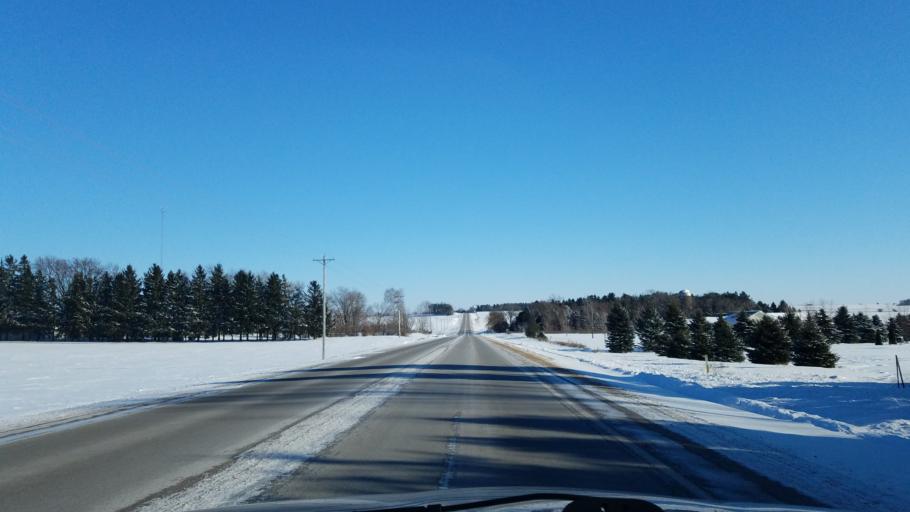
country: US
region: Wisconsin
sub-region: Saint Croix County
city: New Richmond
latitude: 45.0790
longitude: -92.5129
